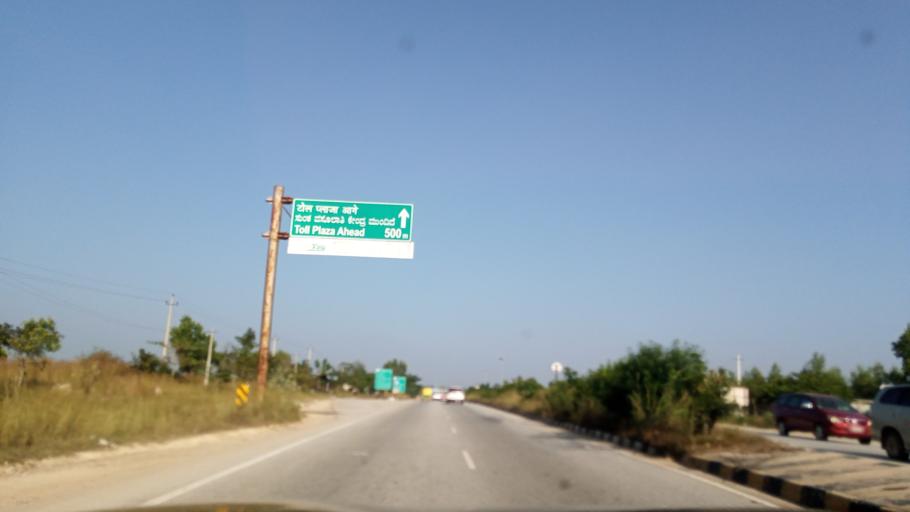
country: IN
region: Karnataka
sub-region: Kolar
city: Mulbagal
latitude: 13.1462
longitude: 78.2850
